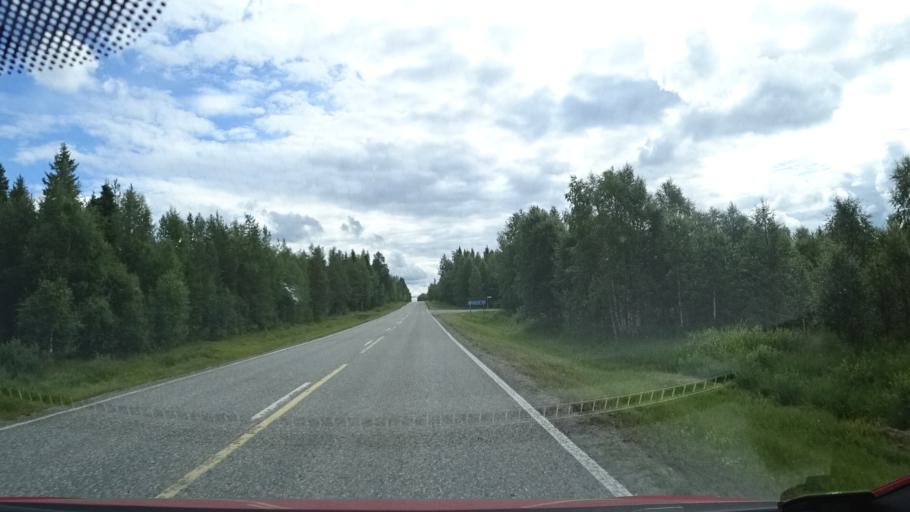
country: FI
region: Lapland
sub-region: Tunturi-Lappi
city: Kittilae
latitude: 67.4757
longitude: 24.9356
